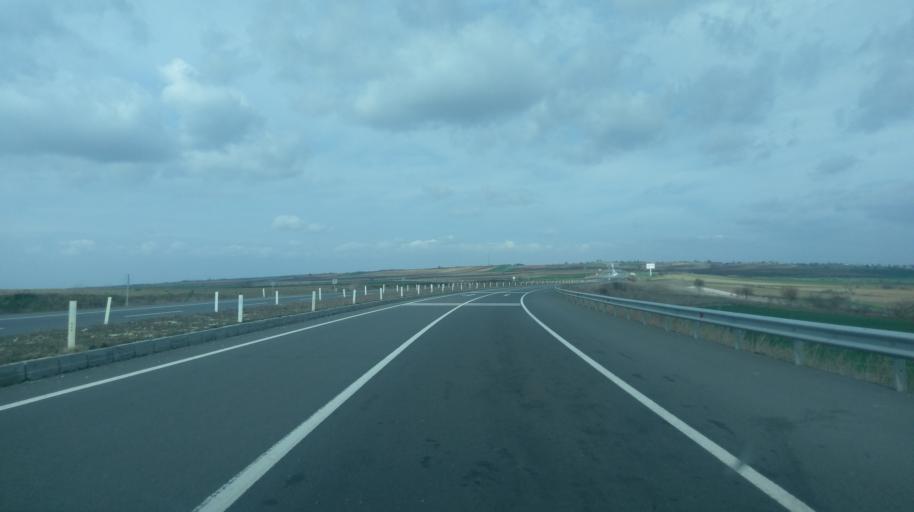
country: TR
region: Edirne
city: Hamidiye
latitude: 41.0394
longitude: 26.6335
